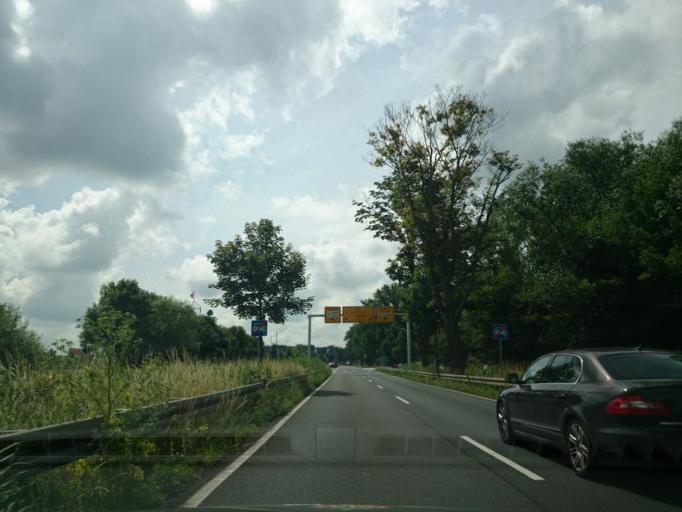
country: DE
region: Brandenburg
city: Rangsdorf
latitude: 52.3015
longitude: 13.4533
